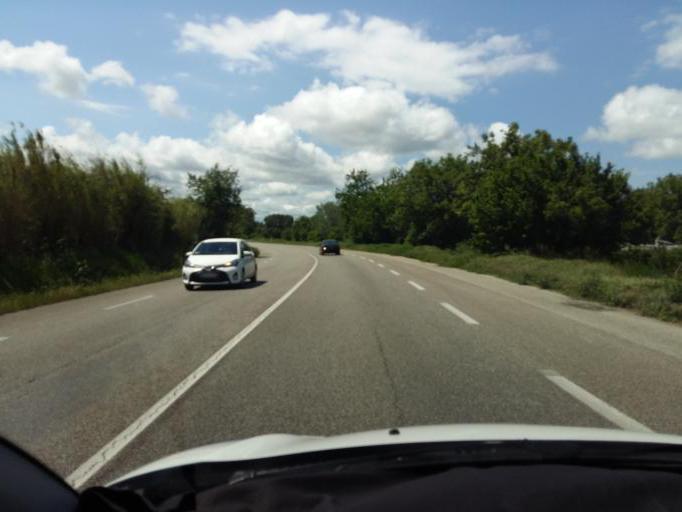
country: FR
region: Provence-Alpes-Cote d'Azur
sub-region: Departement des Bouches-du-Rhone
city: Senas
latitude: 43.7391
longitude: 5.1226
